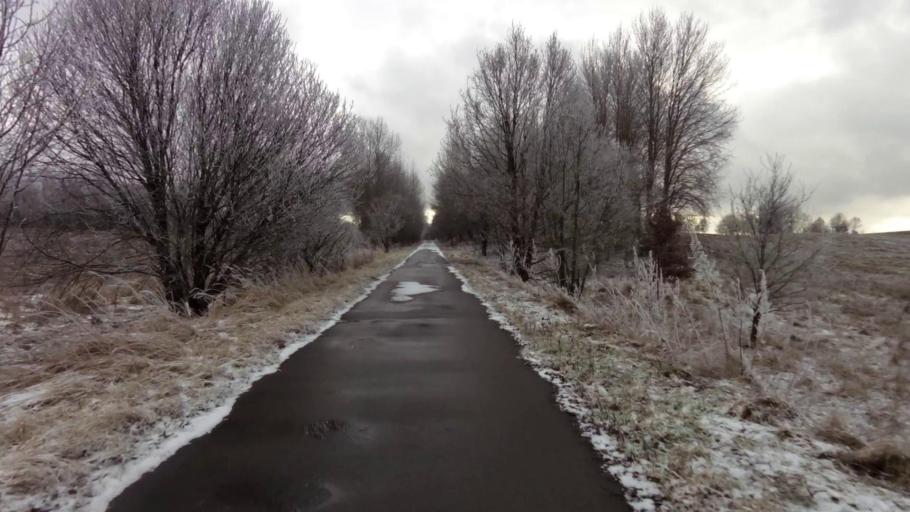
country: PL
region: West Pomeranian Voivodeship
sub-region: Powiat swidwinski
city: Polczyn-Zdroj
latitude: 53.6796
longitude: 16.0318
